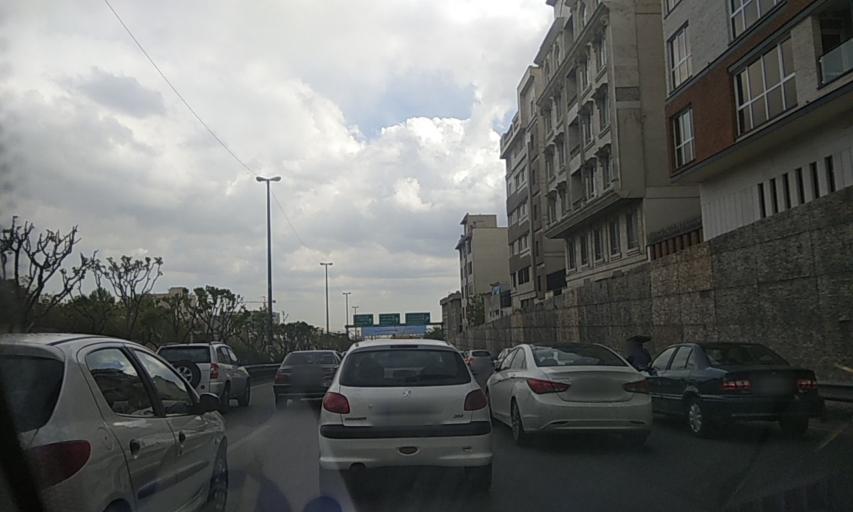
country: IR
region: Tehran
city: Tajrish
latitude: 35.7752
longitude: 51.3442
